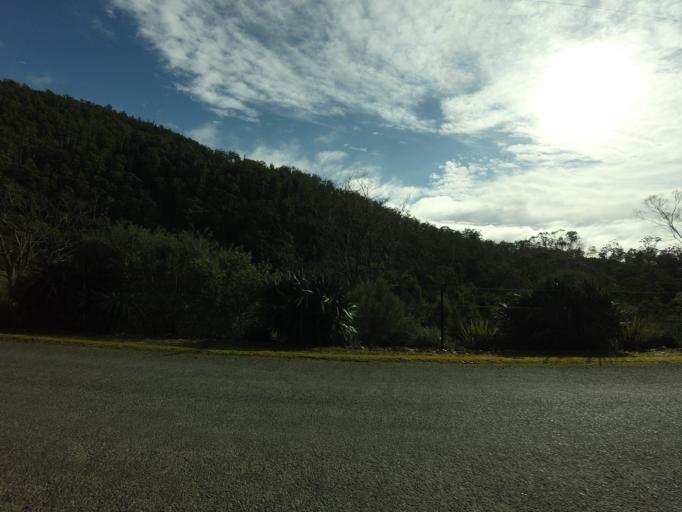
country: AU
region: Tasmania
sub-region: Derwent Valley
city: New Norfolk
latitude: -42.7811
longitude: 146.9495
